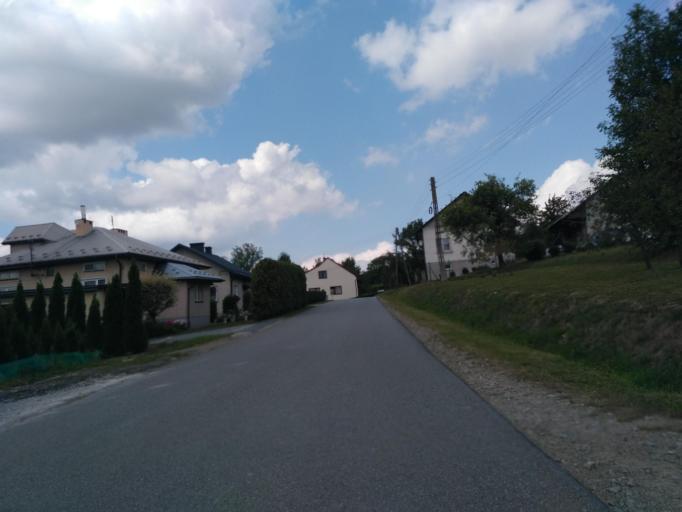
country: PL
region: Subcarpathian Voivodeship
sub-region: Powiat krosnienski
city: Iwonicz-Zdroj
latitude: 49.5880
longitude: 21.7388
